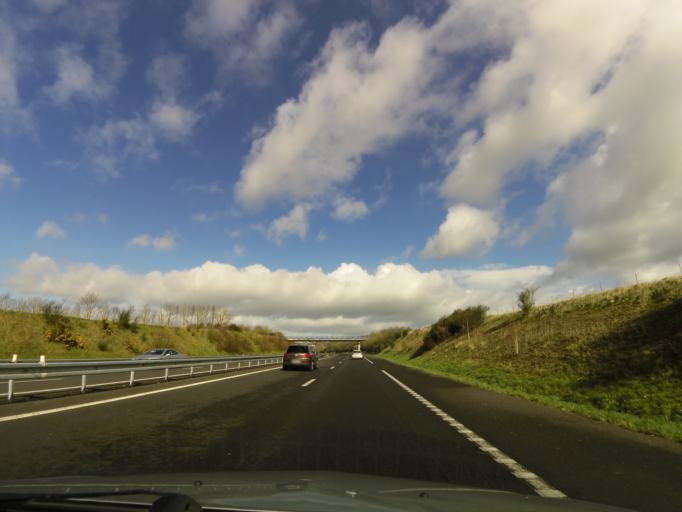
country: FR
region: Lower Normandy
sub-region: Departement de la Manche
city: Conde-sur-Vire
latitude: 49.0619
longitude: -1.0120
